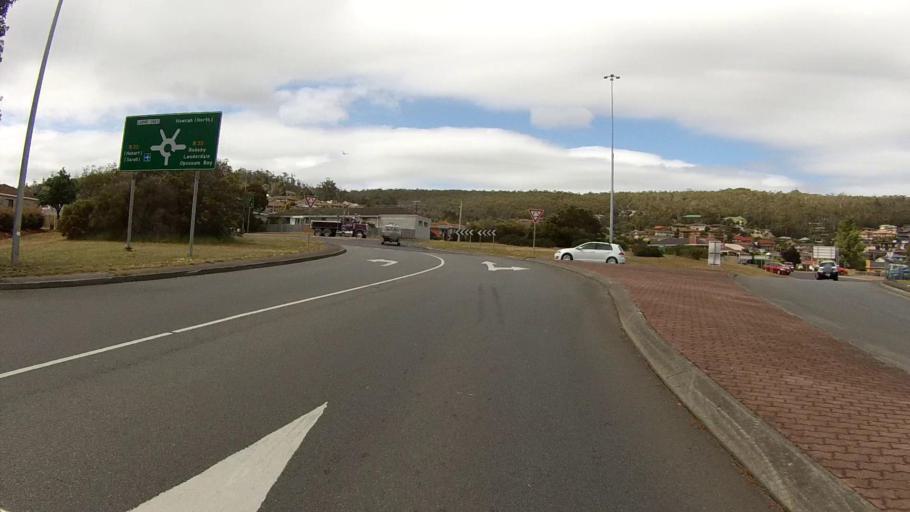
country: AU
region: Tasmania
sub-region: Clarence
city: Howrah
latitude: -42.8785
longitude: 147.4061
